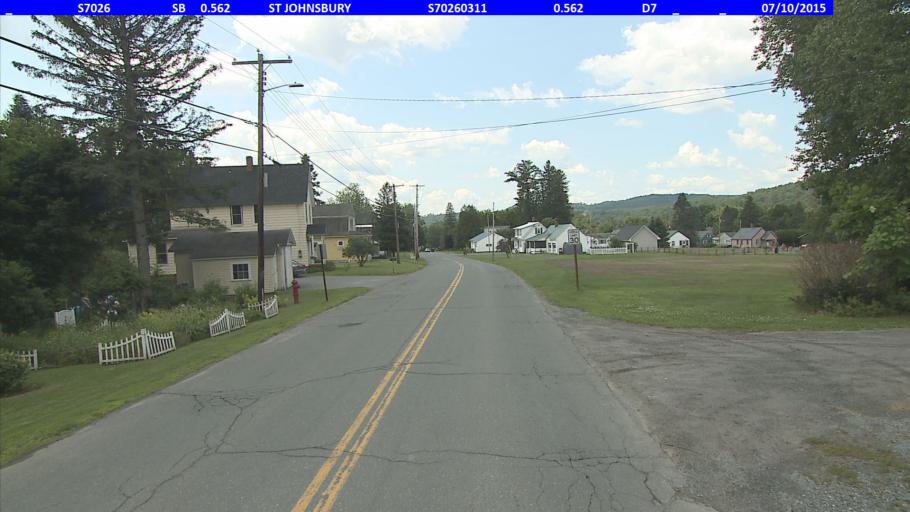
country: US
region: Vermont
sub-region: Caledonia County
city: St Johnsbury
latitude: 44.4329
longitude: -72.0099
